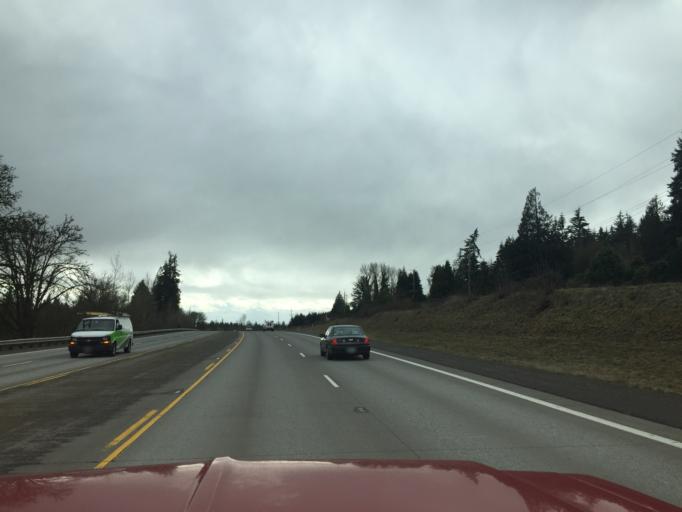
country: US
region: Oregon
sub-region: Columbia County
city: Columbia City
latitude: 45.8830
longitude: -122.8113
